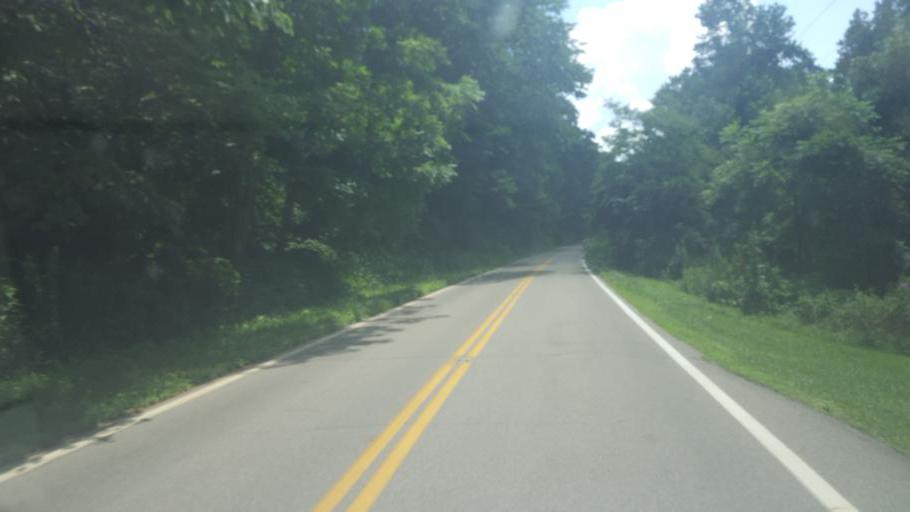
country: US
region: Ohio
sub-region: Ross County
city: Kingston
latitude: 39.4024
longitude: -82.7371
